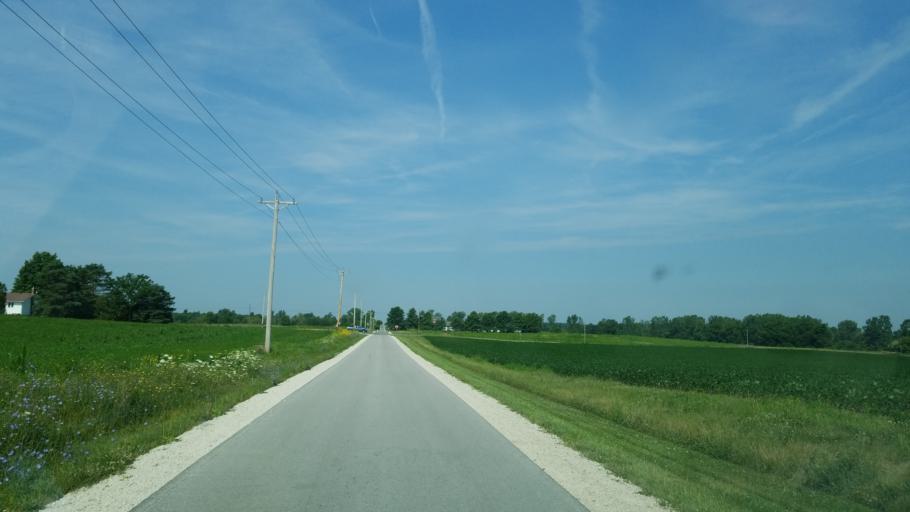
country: US
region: Ohio
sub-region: Sandusky County
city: Green Springs
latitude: 41.1392
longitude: -83.0131
